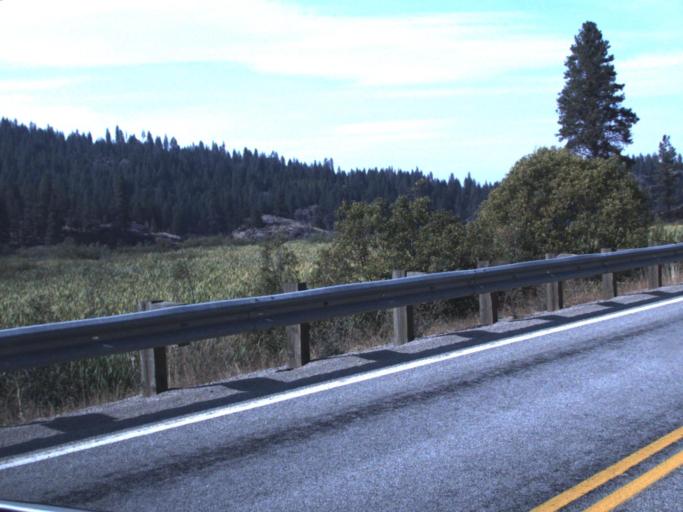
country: US
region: Washington
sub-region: Pend Oreille County
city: Newport
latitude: 48.2157
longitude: -117.2916
